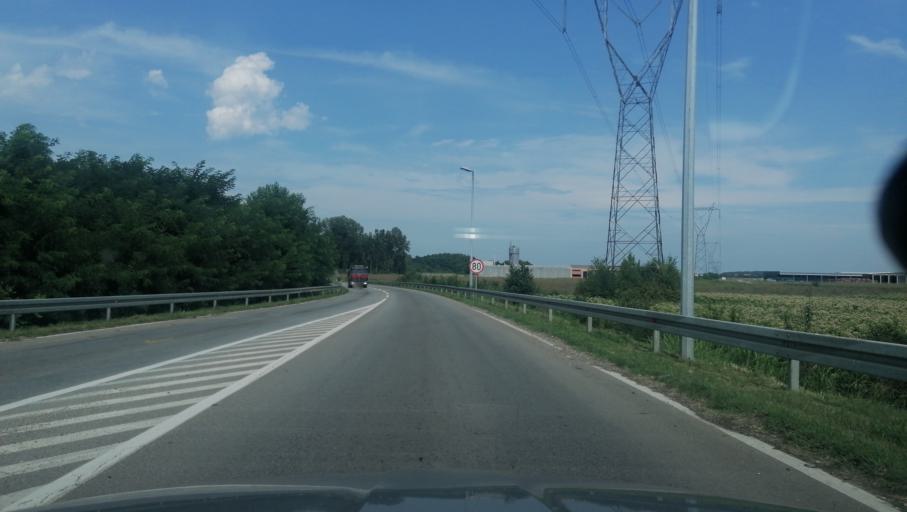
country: BA
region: Republika Srpska
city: Velika Obarska
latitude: 44.7671
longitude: 19.1747
